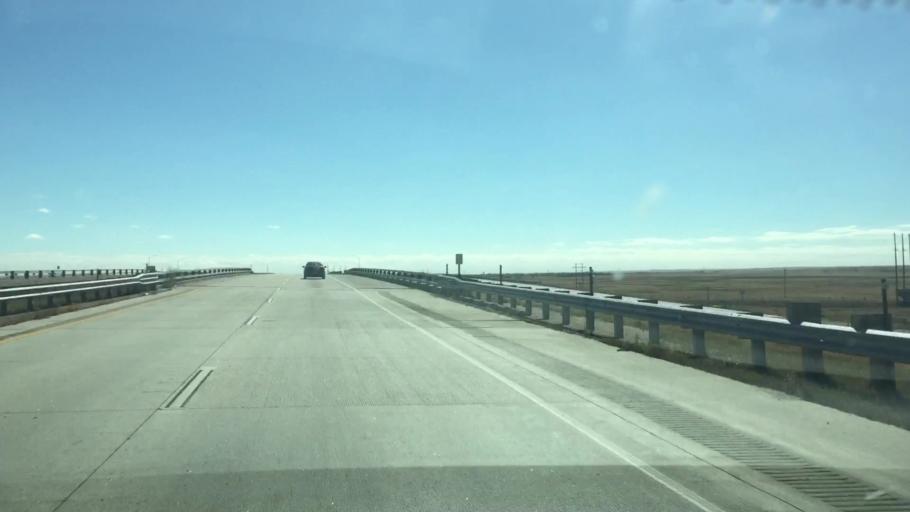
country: US
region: Colorado
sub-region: Lincoln County
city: Limon
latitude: 39.2651
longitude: -103.6691
